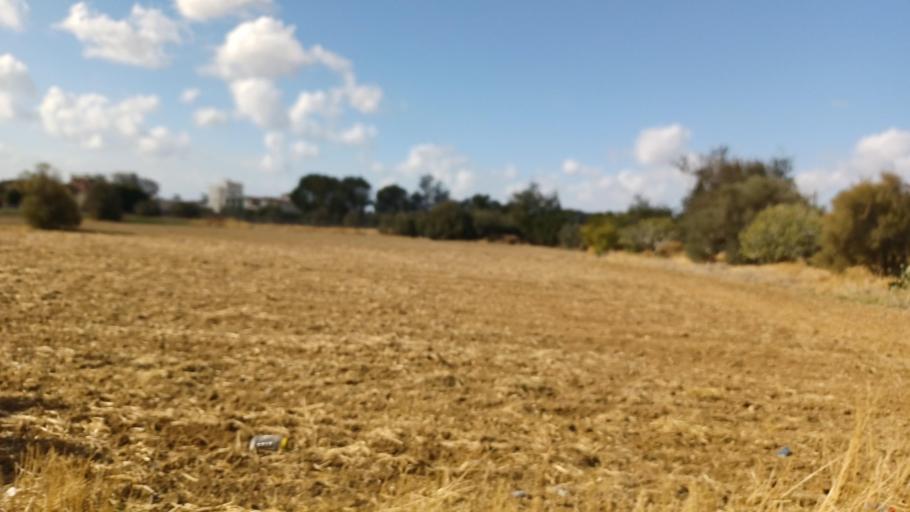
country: CY
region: Limassol
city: Pano Polemidia
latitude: 34.6998
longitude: 33.0005
